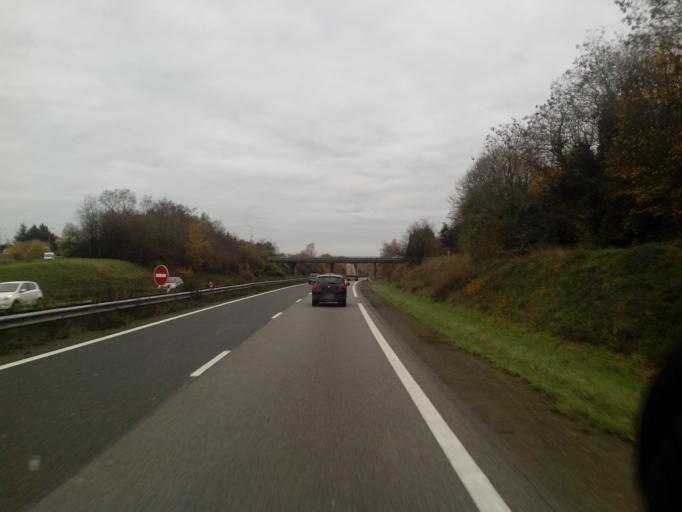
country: FR
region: Pays de la Loire
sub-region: Departement de la Loire-Atlantique
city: Vallet
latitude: 47.1565
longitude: -1.2773
